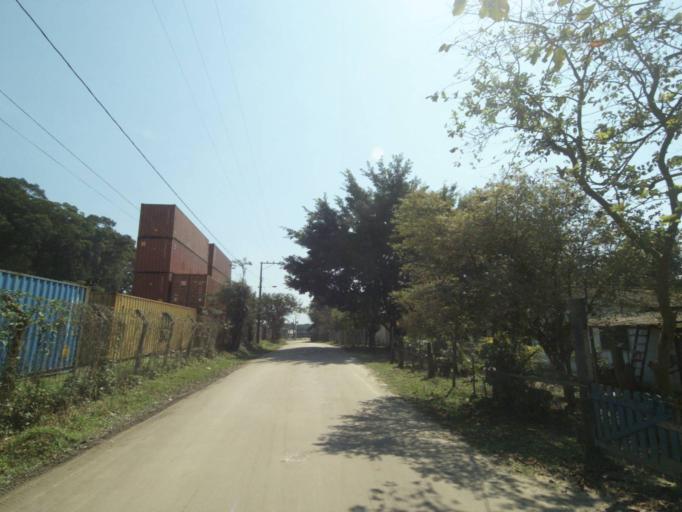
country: BR
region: Parana
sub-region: Paranagua
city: Paranagua
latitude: -25.5520
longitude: -48.5904
